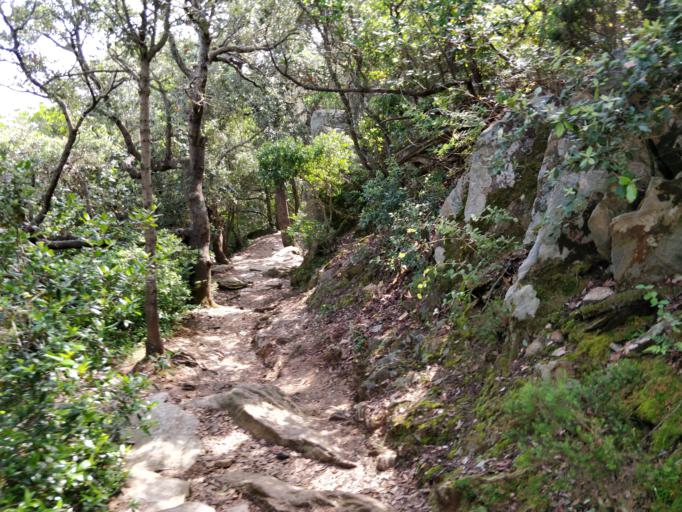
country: FR
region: Provence-Alpes-Cote d'Azur
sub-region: Departement du Var
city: Le Lavandou
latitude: 43.0114
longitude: 6.3879
